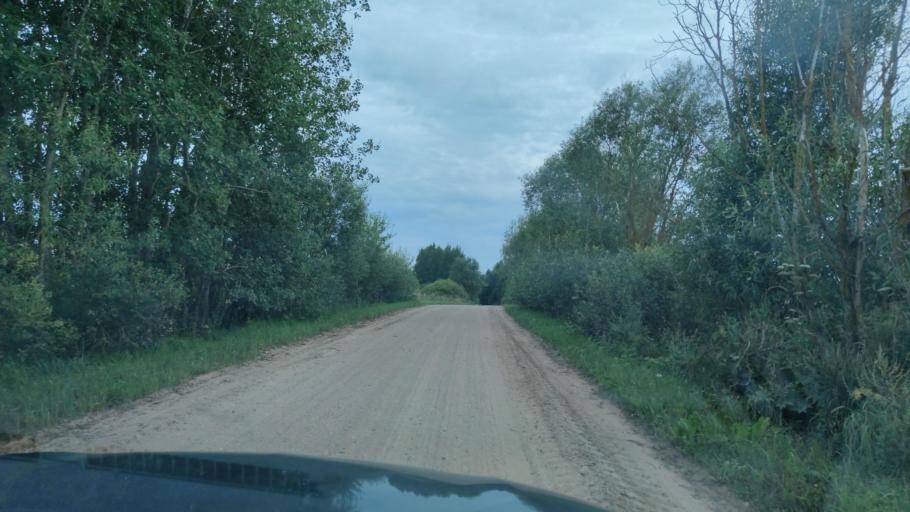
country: BY
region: Vitebsk
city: Pastavy
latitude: 55.1162
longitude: 27.1481
